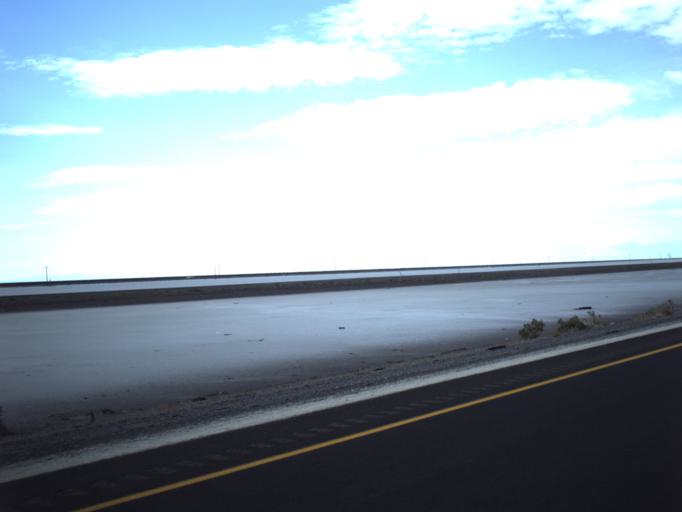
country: US
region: Utah
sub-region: Tooele County
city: Wendover
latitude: 40.7332
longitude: -113.5575
